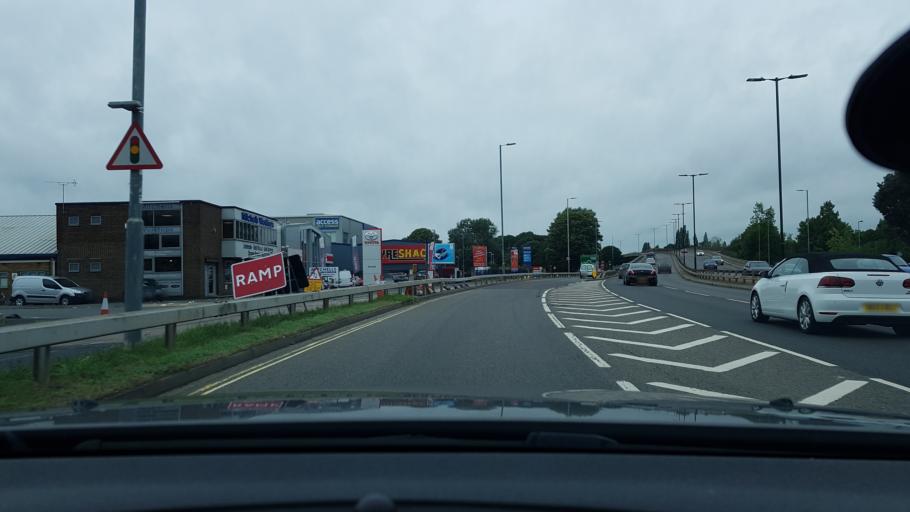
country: GB
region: England
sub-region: Hampshire
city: Marchwood
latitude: 50.9153
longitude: -1.4535
